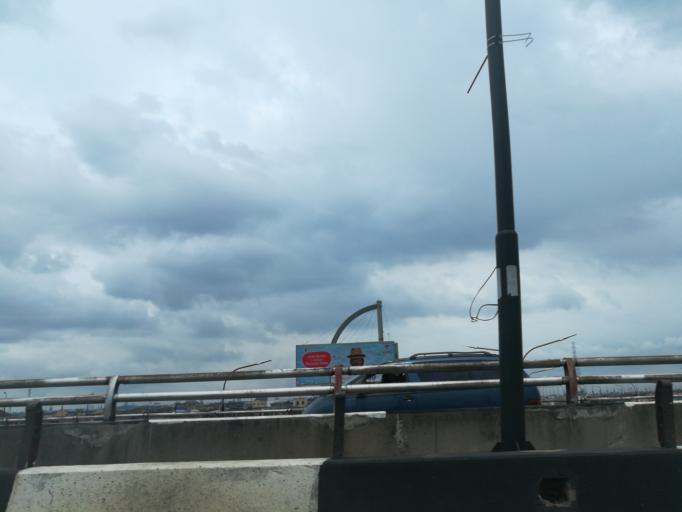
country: NG
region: Lagos
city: Lagos
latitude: 6.4614
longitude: 3.3962
